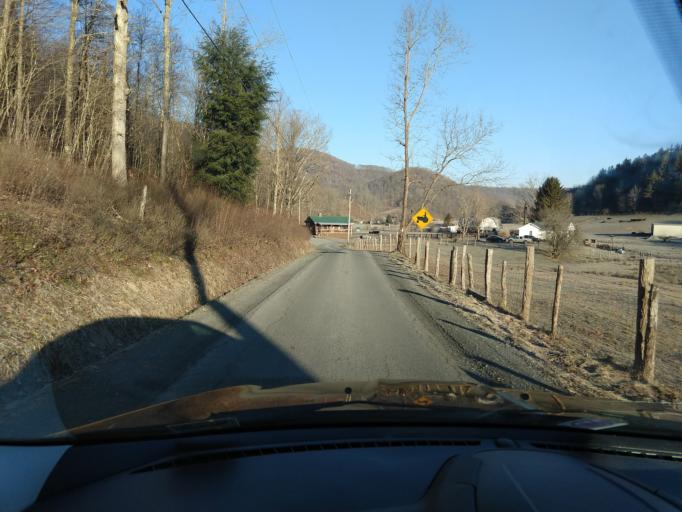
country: US
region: West Virginia
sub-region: Greenbrier County
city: Rainelle
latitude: 37.9145
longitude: -80.7538
